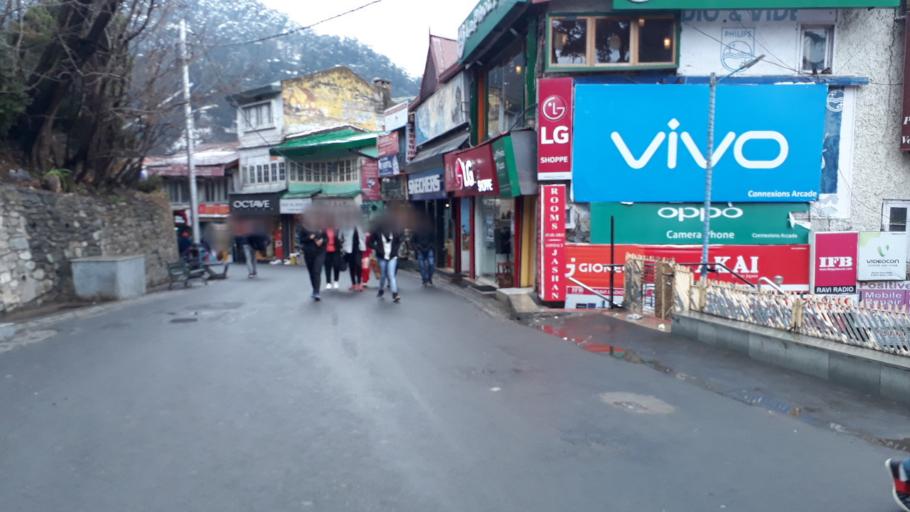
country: IN
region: Himachal Pradesh
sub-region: Shimla
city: Shimla
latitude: 31.1042
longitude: 77.1754
